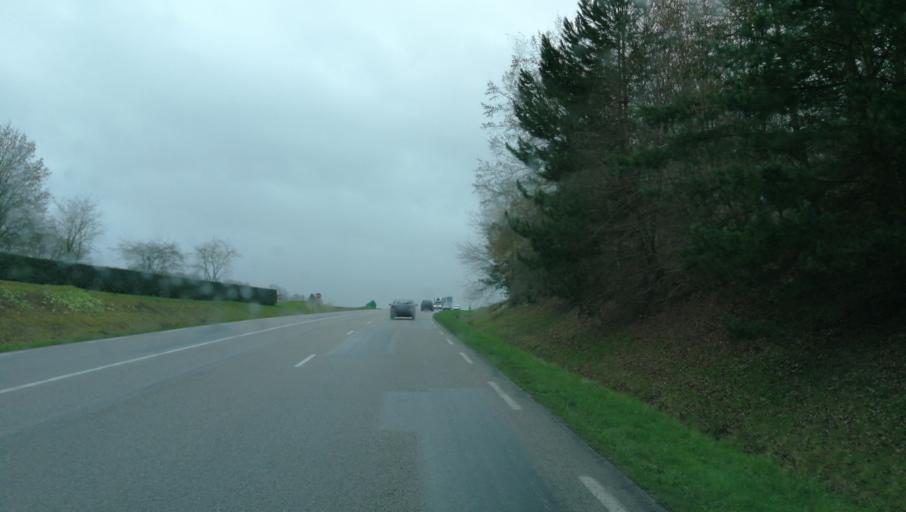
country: FR
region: Haute-Normandie
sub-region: Departement de l'Eure
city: Brionne
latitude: 49.1835
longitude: 0.7067
